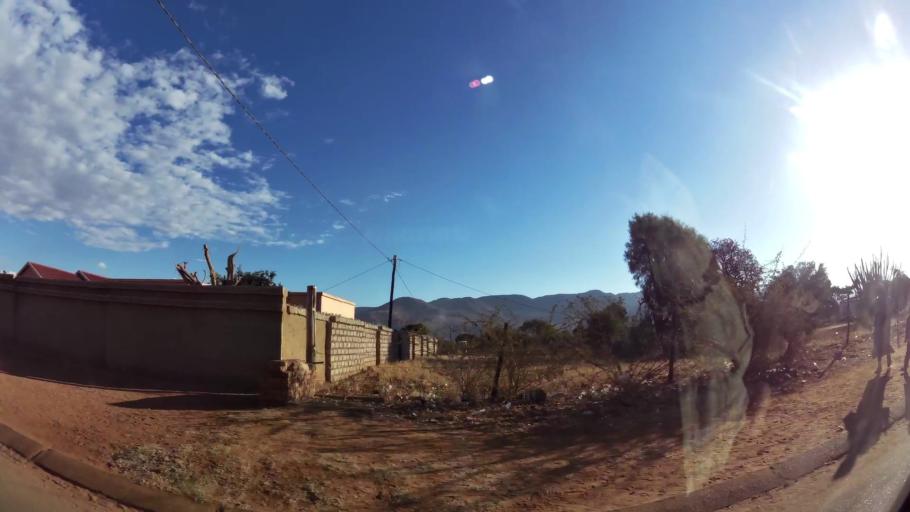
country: ZA
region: Limpopo
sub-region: Waterberg District Municipality
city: Mokopane
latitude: -24.1716
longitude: 28.9792
